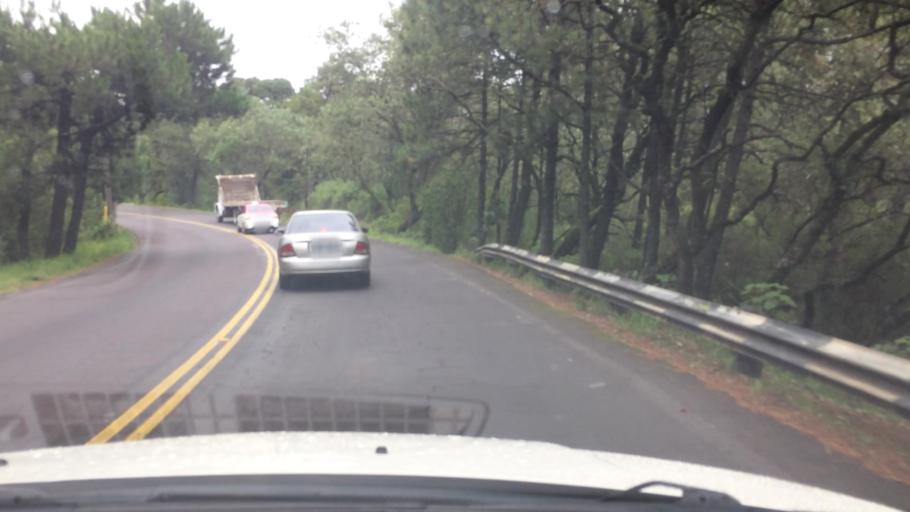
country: MX
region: Mexico City
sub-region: Tlalpan
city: Lomas de Tepemecatl
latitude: 19.2591
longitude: -99.2377
